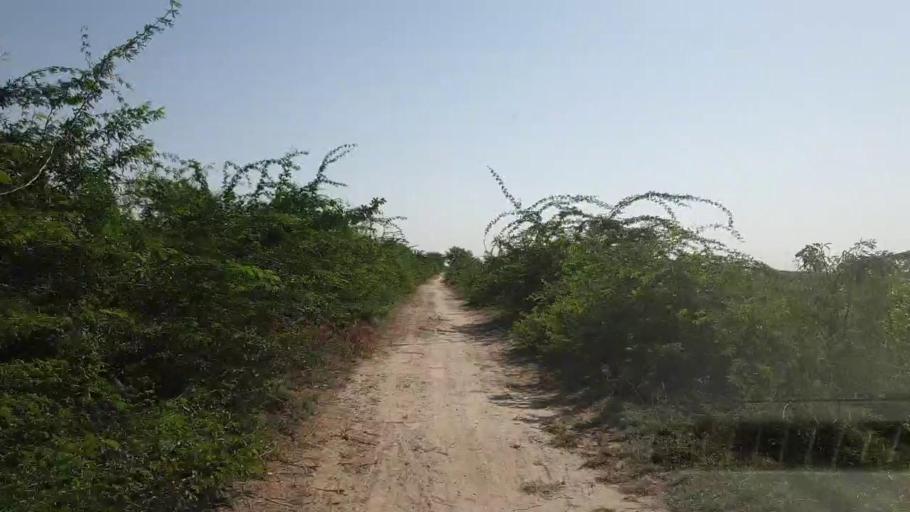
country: PK
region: Sindh
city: Kadhan
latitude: 24.5986
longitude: 69.0051
